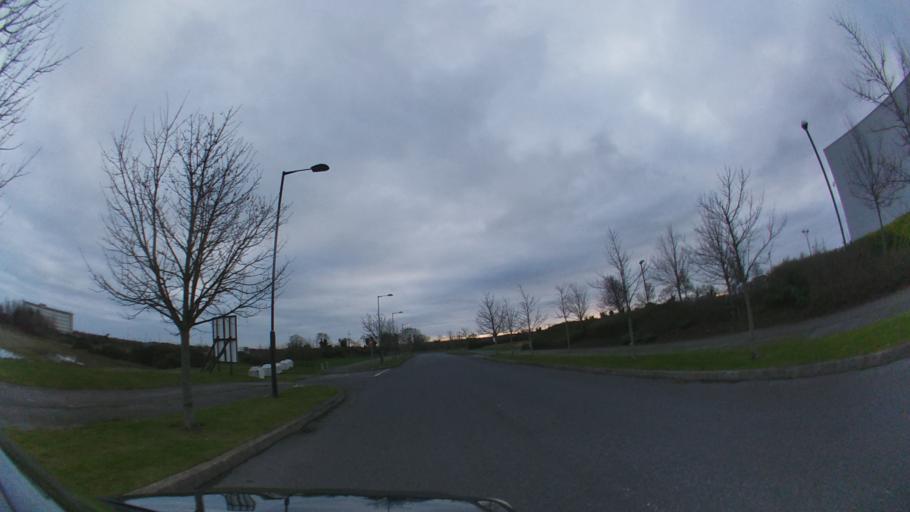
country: IE
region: Leinster
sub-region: An Mhi
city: Stamullin
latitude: 53.6383
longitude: -6.2628
